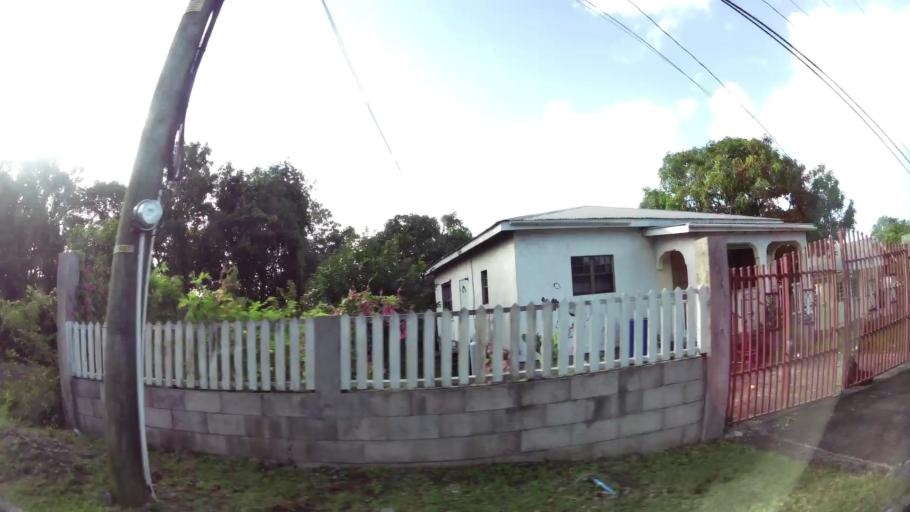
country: KN
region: Saint John Figtree
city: Fig Tree
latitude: 17.1284
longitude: -62.6045
